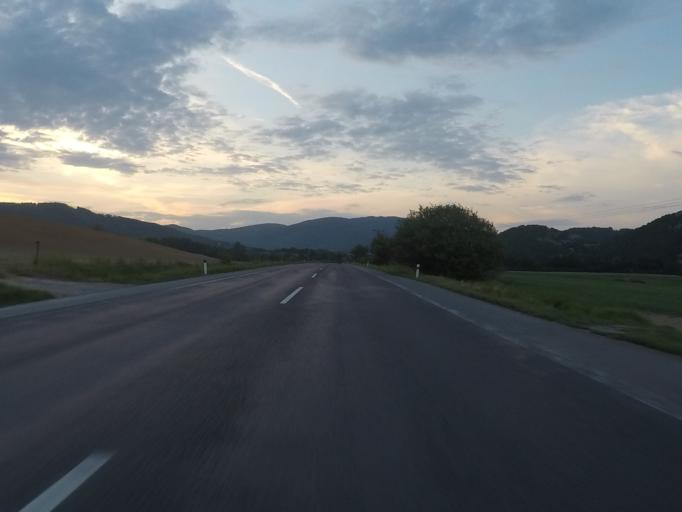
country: SK
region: Banskobystricky
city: Rimavska Sobota
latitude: 48.4860
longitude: 19.9442
